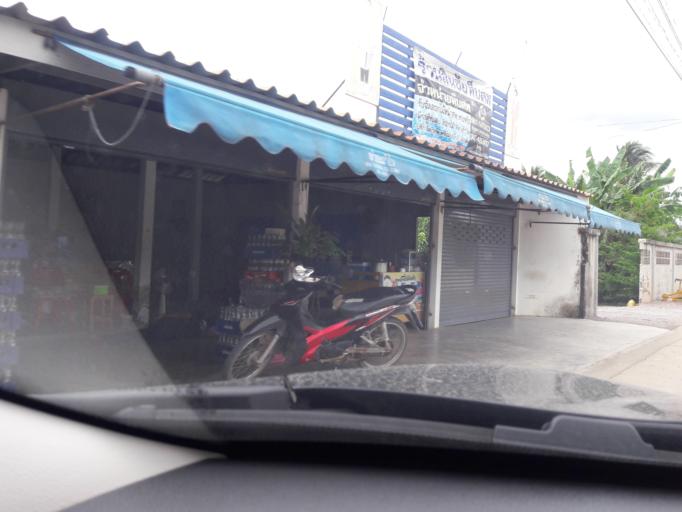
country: TH
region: Ratchaburi
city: Bang Phae
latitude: 13.6044
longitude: 99.9064
